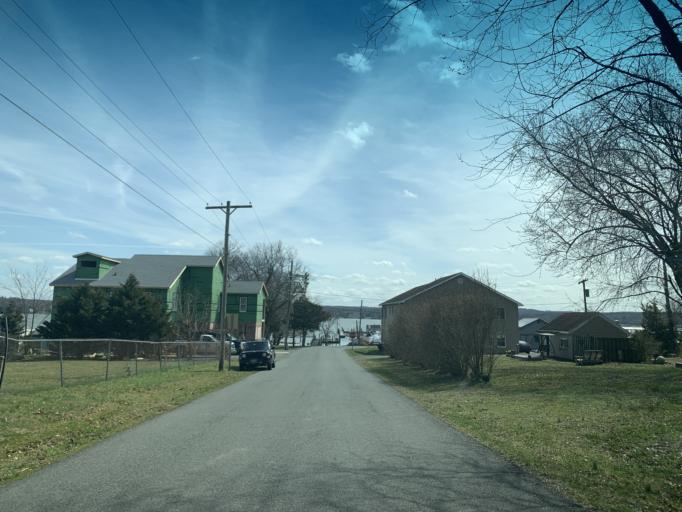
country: US
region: Maryland
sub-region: Cecil County
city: Charlestown
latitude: 39.5754
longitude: -75.9708
